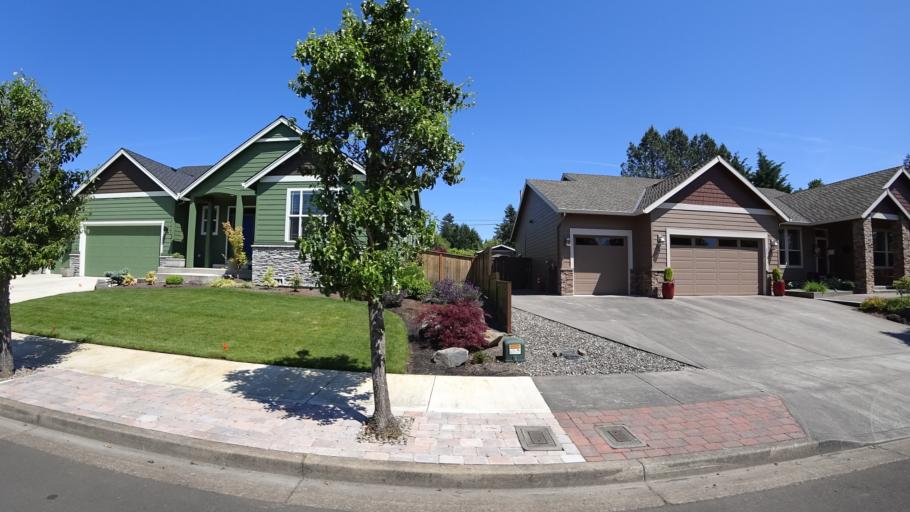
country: US
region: Oregon
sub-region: Clackamas County
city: Happy Valley
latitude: 45.4766
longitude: -122.4859
